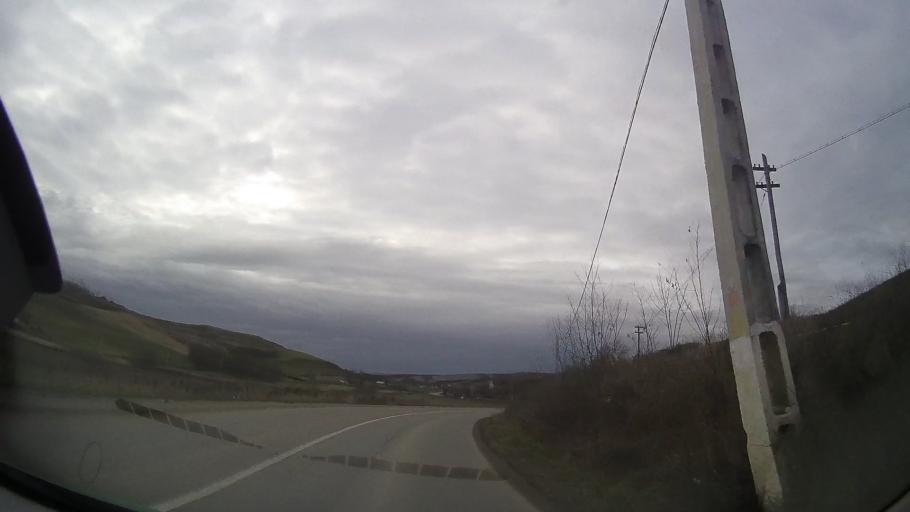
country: RO
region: Bistrita-Nasaud
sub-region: Comuna Budesti
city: Budesti
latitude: 46.8522
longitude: 24.2428
